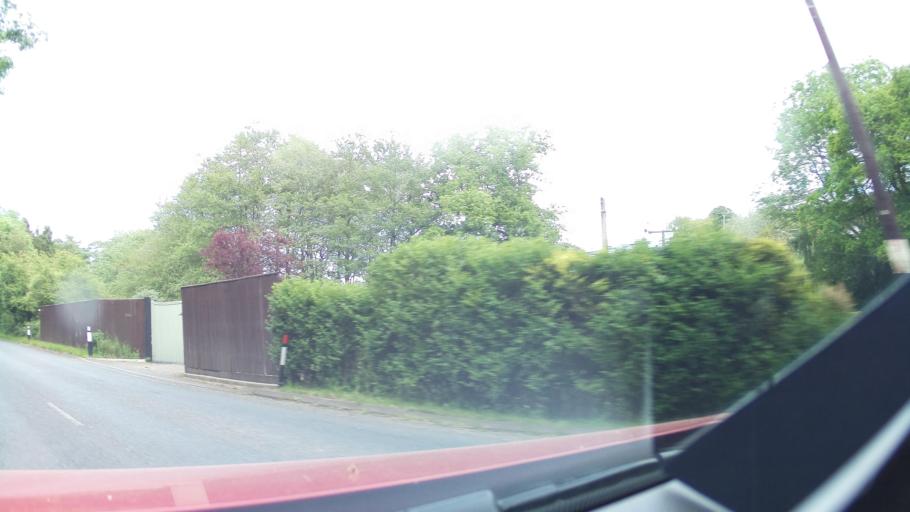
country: GB
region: England
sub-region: Worcestershire
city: Great Malvern
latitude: 52.1394
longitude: -2.3562
